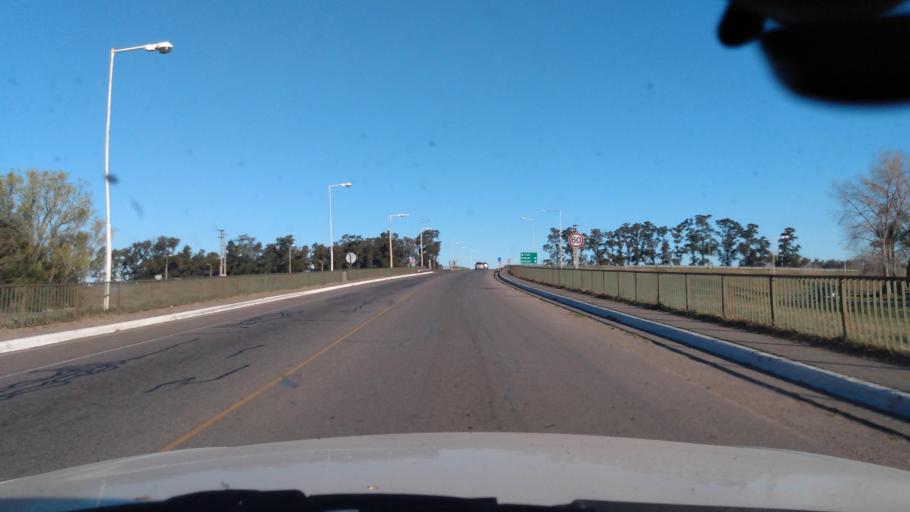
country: AR
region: Buenos Aires
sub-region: Partido de Lujan
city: Lujan
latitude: -34.6308
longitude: -59.2505
